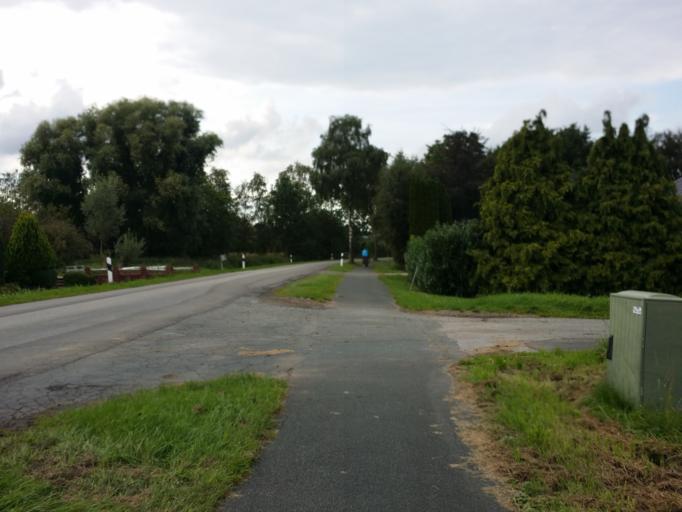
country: DE
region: Lower Saxony
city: Oederquart
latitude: 53.7825
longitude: 9.2456
